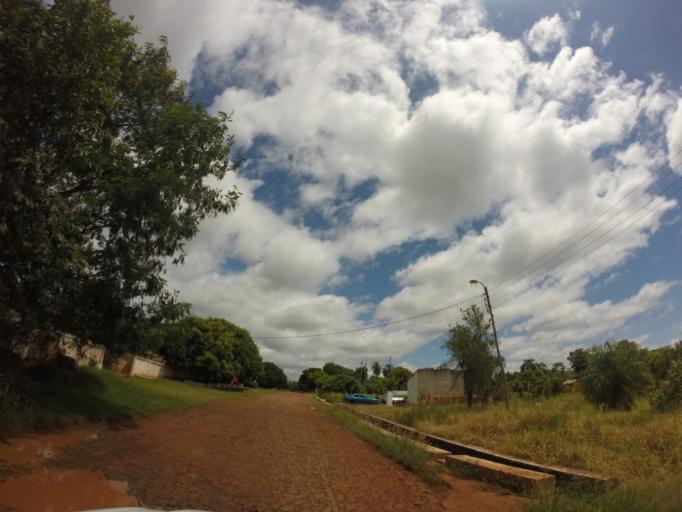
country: PY
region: Alto Parana
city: Ciudad del Este
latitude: -25.3992
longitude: -54.6501
